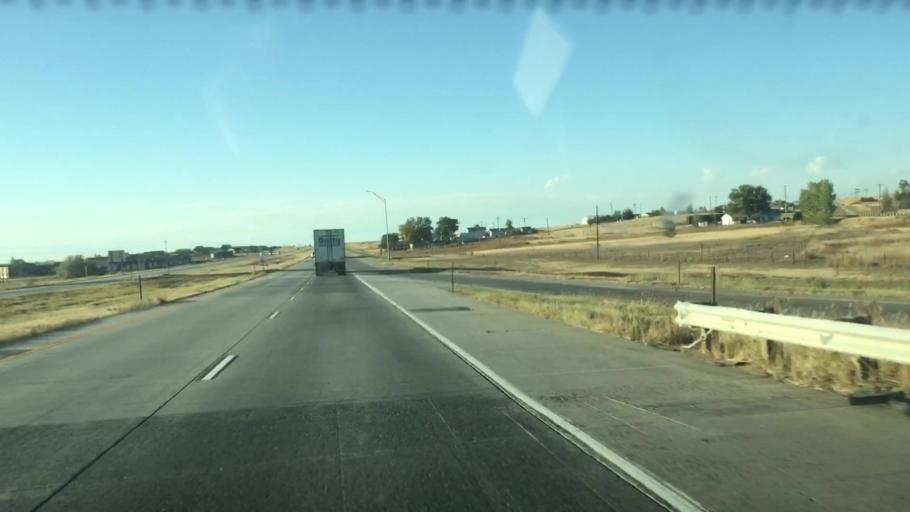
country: US
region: Colorado
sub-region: Arapahoe County
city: Byers
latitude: 39.6180
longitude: -104.0427
